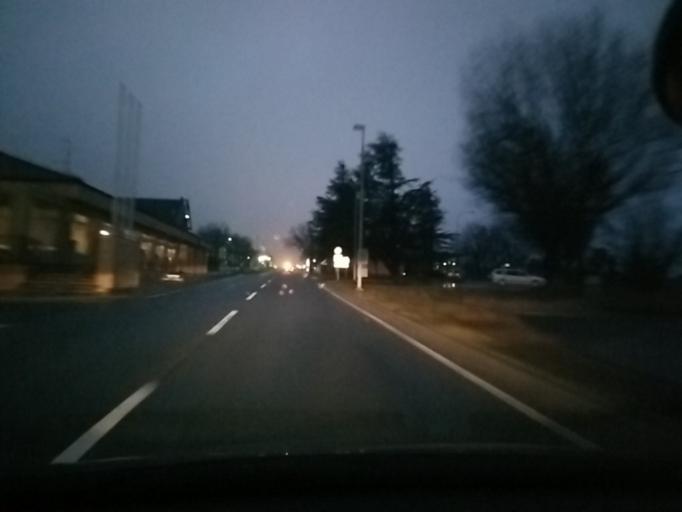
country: SI
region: Hrpelje-Kozina
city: Kozina
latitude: 45.6212
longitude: 13.9058
